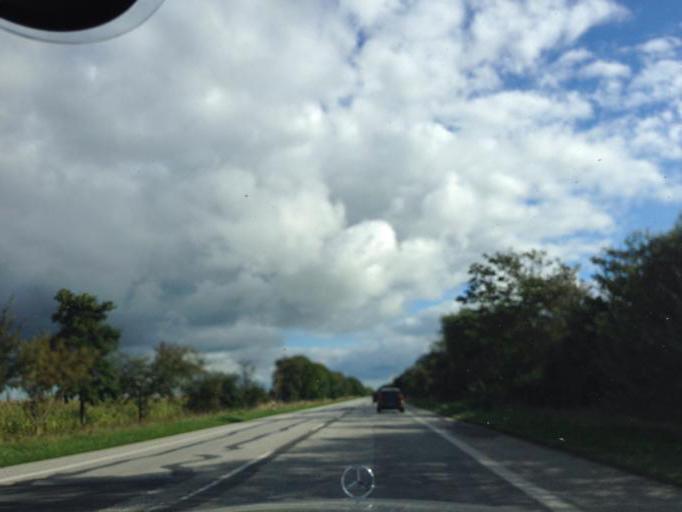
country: DE
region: Schleswig-Holstein
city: Stedesand
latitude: 54.7443
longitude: 8.9207
